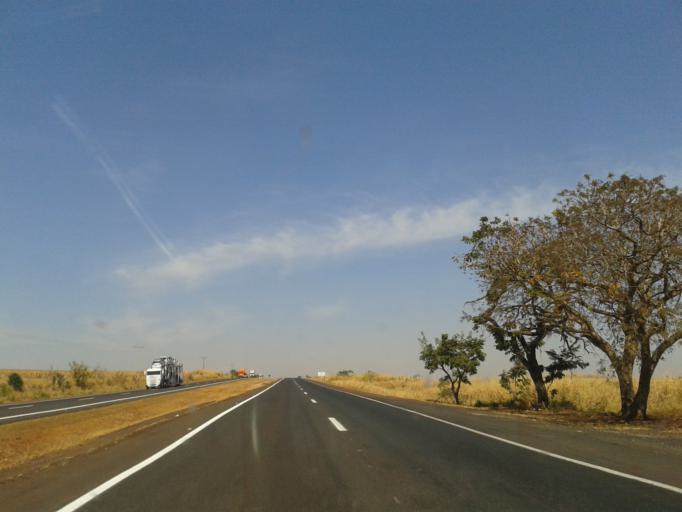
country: BR
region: Goias
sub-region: Goiatuba
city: Goiatuba
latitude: -18.1636
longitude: -49.2883
